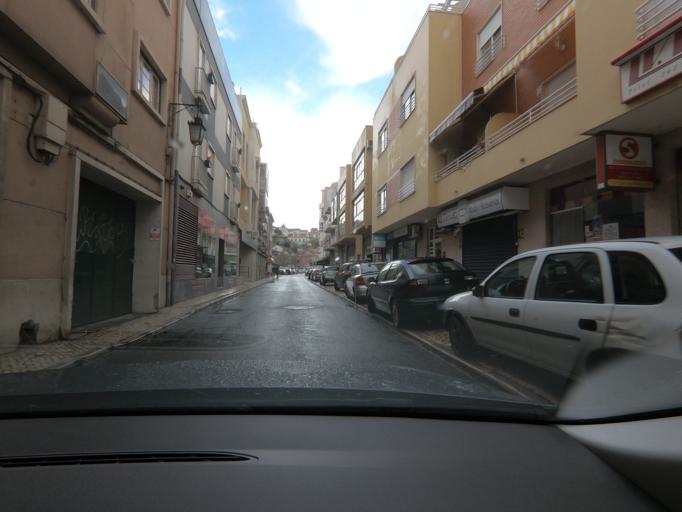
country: PT
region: Lisbon
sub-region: Alenquer
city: Alenquer
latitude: 39.0517
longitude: -9.0076
